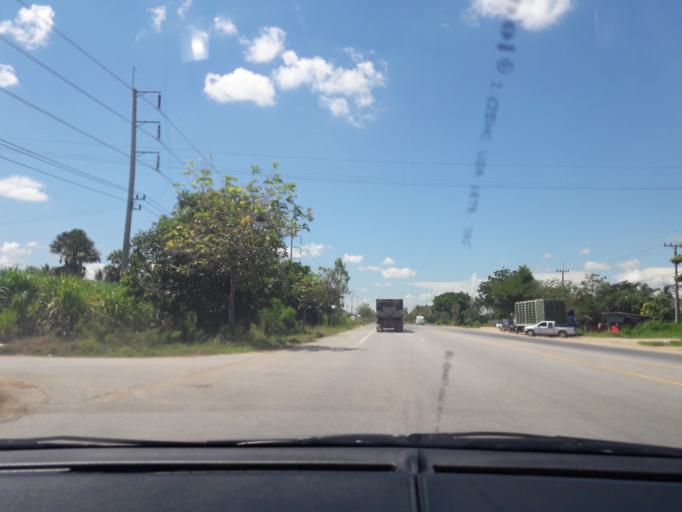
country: TH
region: Kanchanaburi
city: Phanom Thuan
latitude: 14.0463
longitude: 99.7828
